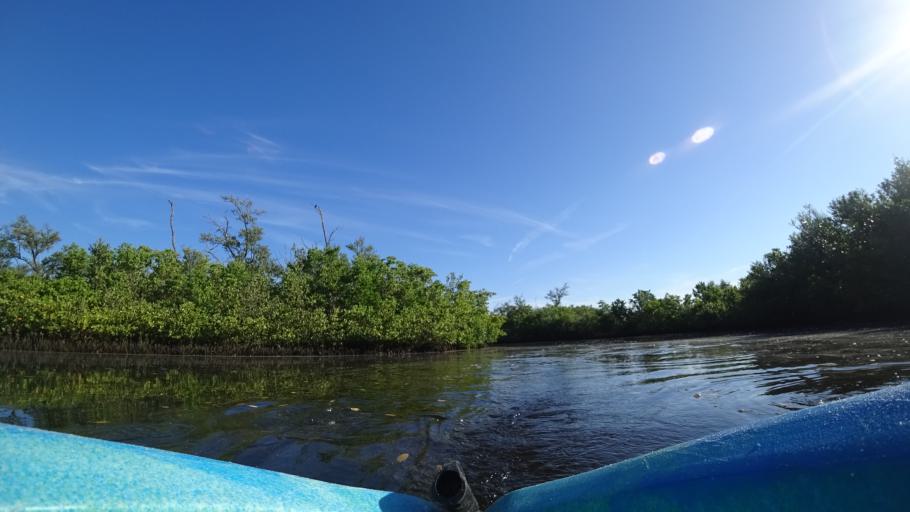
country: US
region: Florida
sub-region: Manatee County
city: Holmes Beach
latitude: 27.5099
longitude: -82.6717
